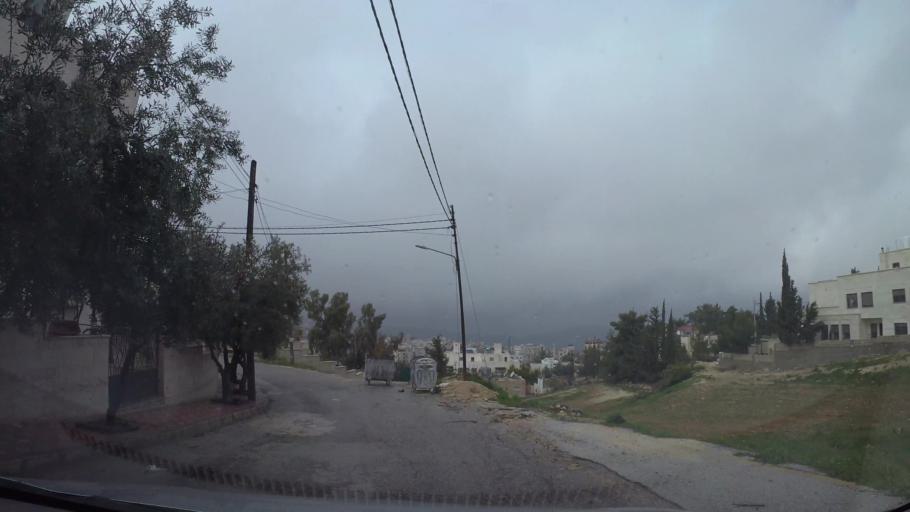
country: JO
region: Amman
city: Al Jubayhah
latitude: 32.0258
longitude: 35.8273
